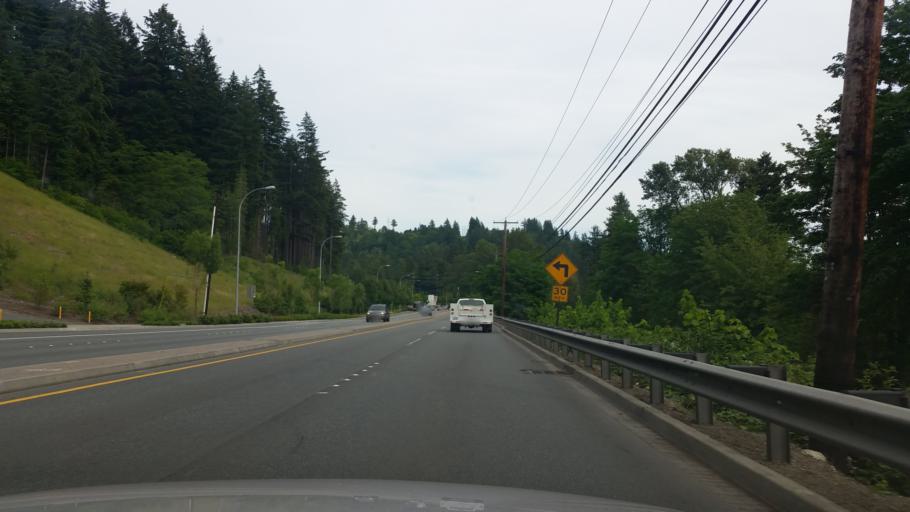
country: US
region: Washington
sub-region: King County
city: Bothell
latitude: 47.7521
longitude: -122.2182
